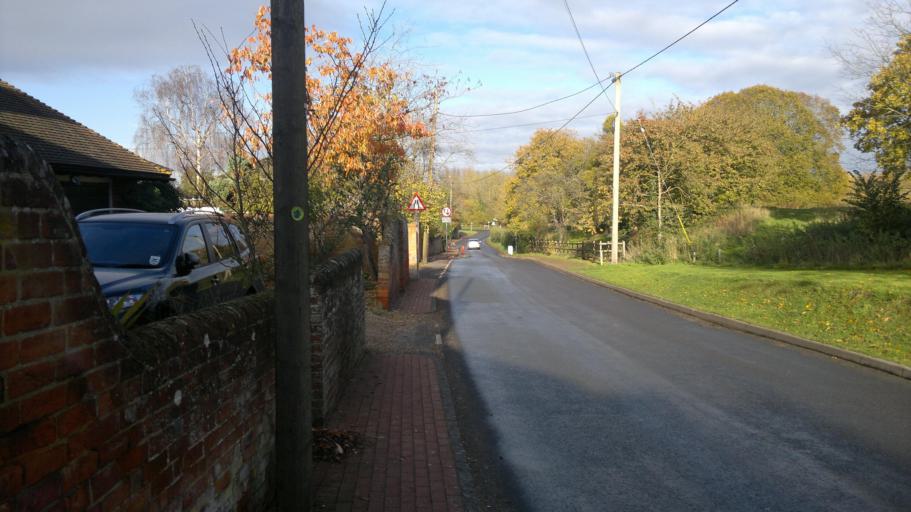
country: GB
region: England
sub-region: Hampshire
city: Old Basing
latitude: 51.2760
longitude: -1.0446
